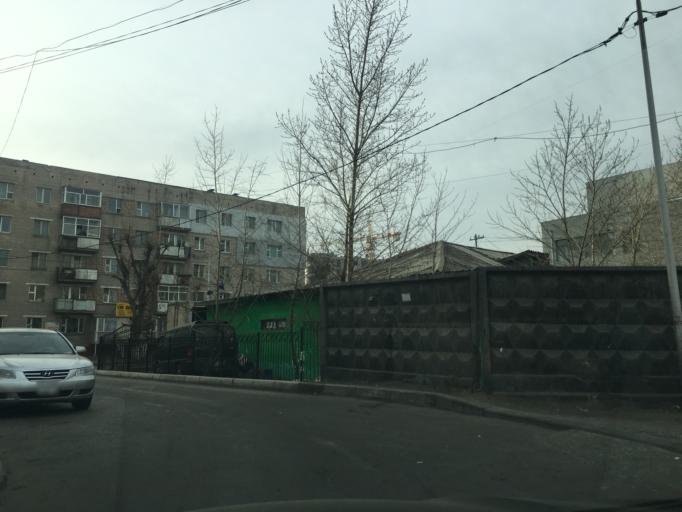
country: MN
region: Ulaanbaatar
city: Ulaanbaatar
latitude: 47.9111
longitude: 106.8878
